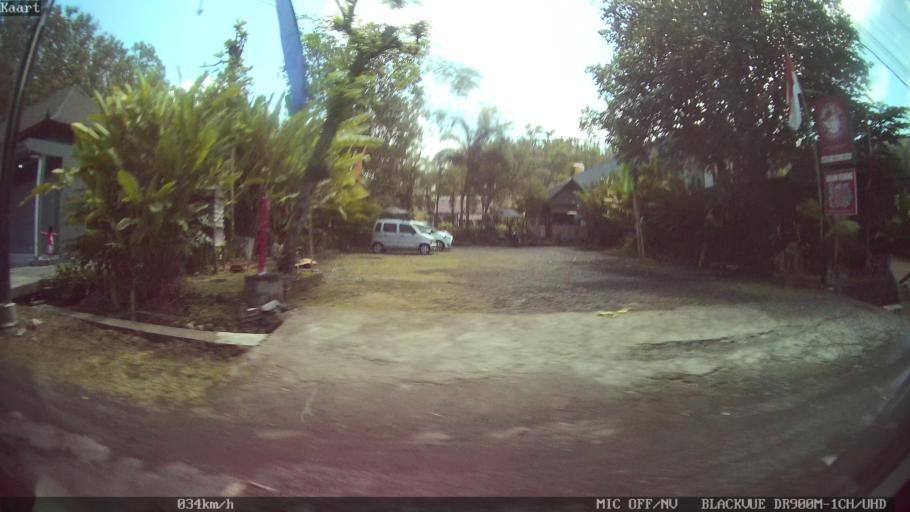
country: ID
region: Bali
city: Banjar Paangkelod
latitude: -8.6120
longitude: 115.2571
